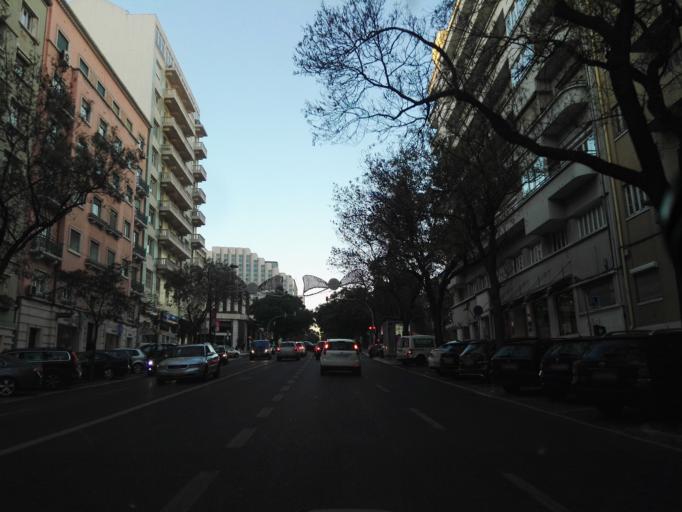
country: PT
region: Lisbon
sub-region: Lisbon
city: Lisbon
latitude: 38.7244
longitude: -9.1529
